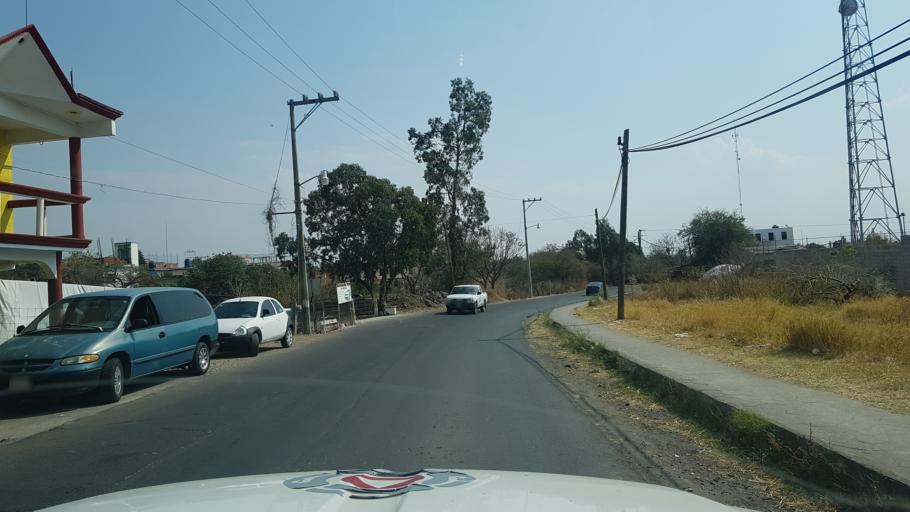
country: MX
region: Morelos
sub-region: Yecapixtla
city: Yecapixtla
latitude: 18.8849
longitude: -98.8669
